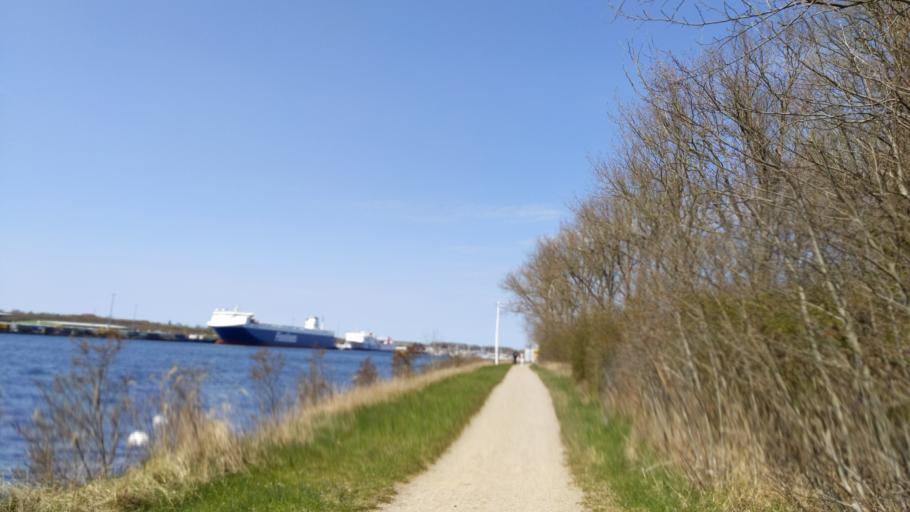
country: DE
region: Schleswig-Holstein
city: Travemuende
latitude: 53.9425
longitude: 10.8655
